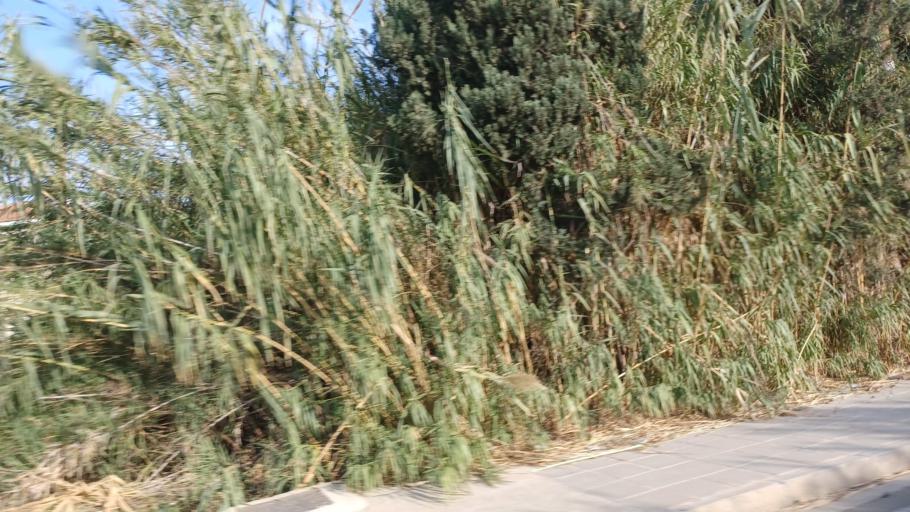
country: CY
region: Ammochostos
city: Acheritou
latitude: 35.0703
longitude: 33.8770
